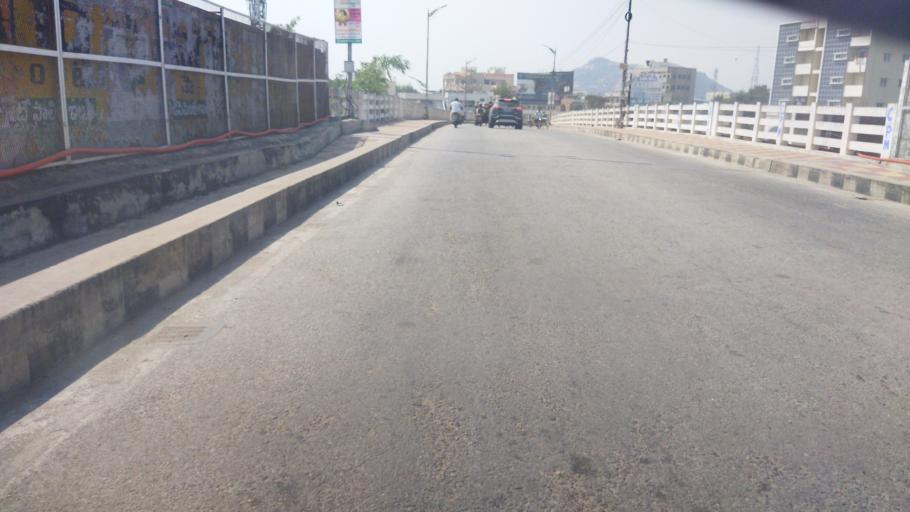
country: IN
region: Telangana
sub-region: Nalgonda
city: Nalgonda
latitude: 17.0651
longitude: 79.2797
